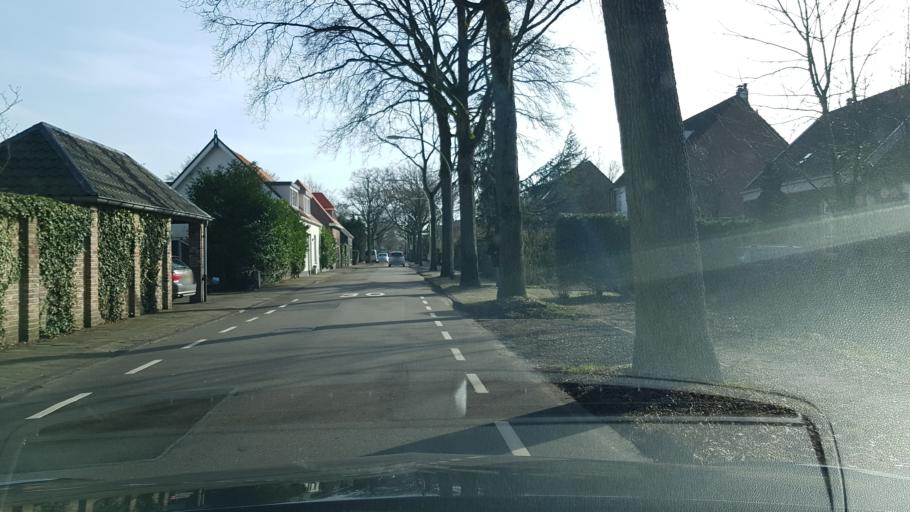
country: NL
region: North Holland
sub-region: Gemeente Bloemendaal
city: Bennebroek
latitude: 52.3305
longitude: 4.6048
